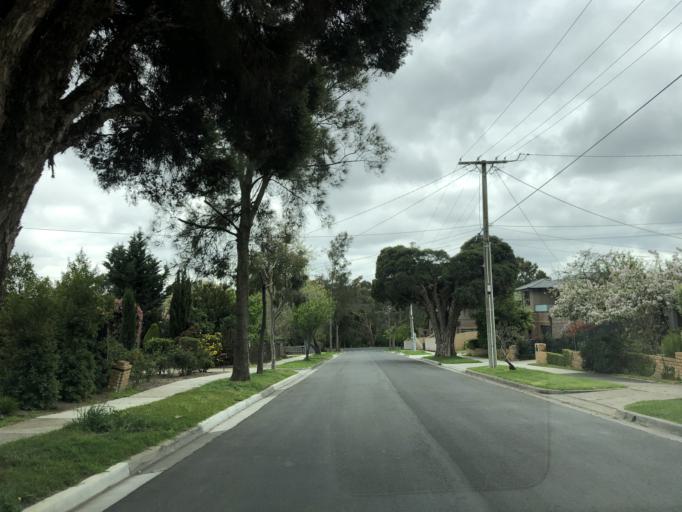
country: AU
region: Victoria
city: Burwood East
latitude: -37.8436
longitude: 145.1411
